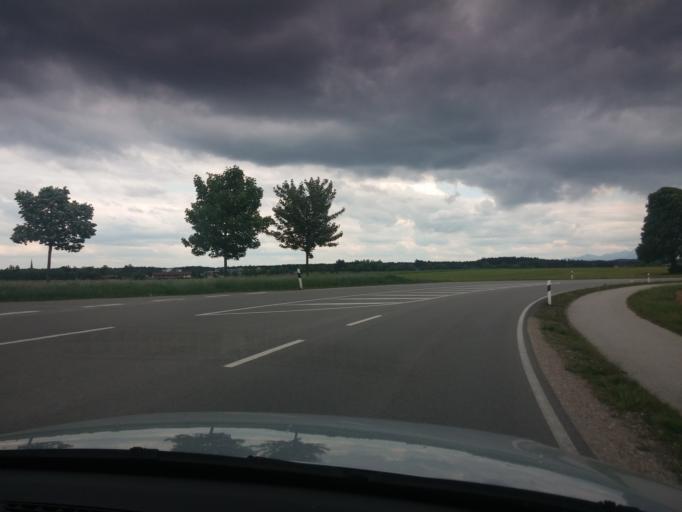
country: DE
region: Bavaria
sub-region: Upper Bavaria
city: Holzkirchen
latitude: 47.8930
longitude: 11.7008
